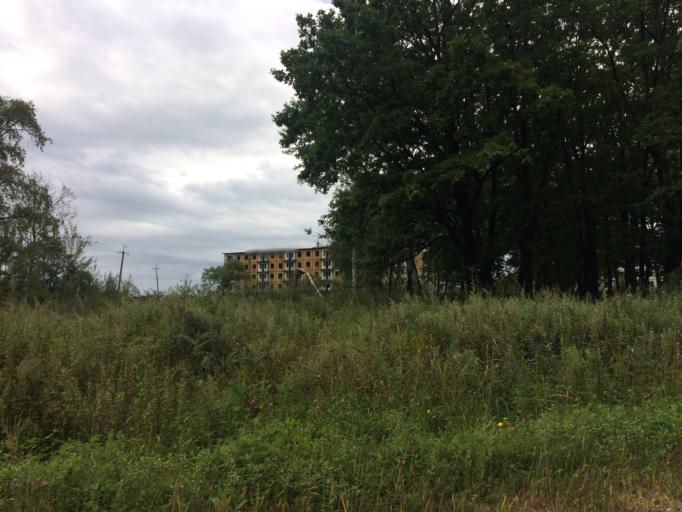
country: RU
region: Primorskiy
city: Lazo
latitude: 45.8226
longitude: 133.6440
